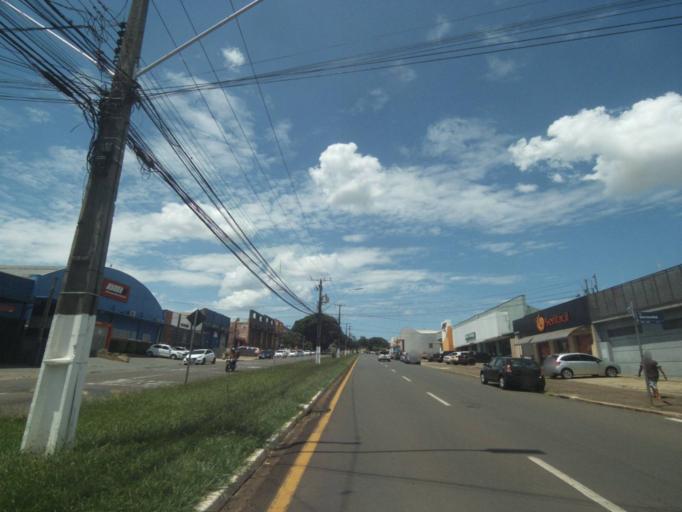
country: BR
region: Parana
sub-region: Londrina
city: Londrina
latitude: -23.3012
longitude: -51.1944
